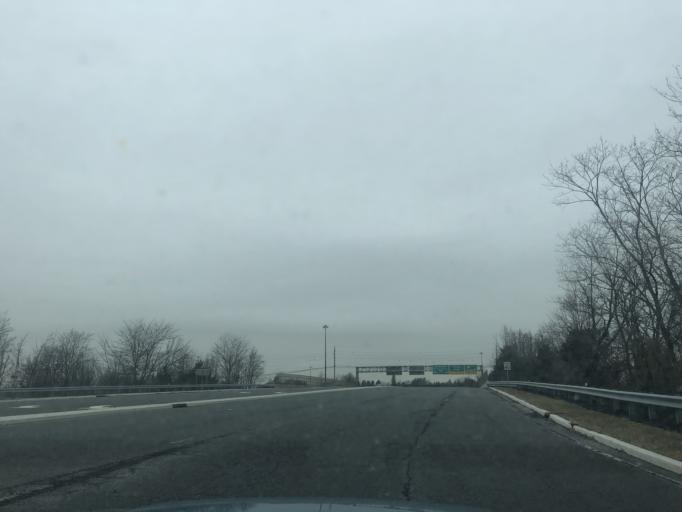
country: US
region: New Jersey
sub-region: Somerset County
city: Kingston
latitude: 40.3565
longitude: -74.6054
